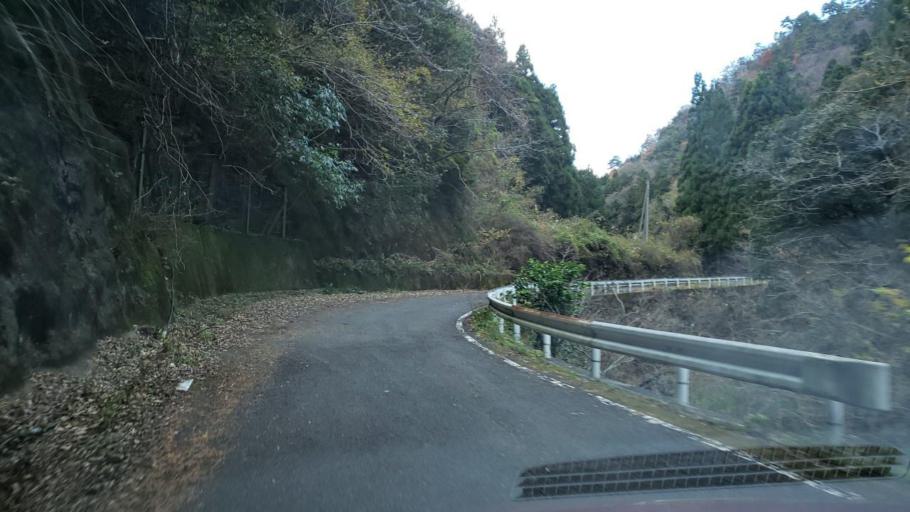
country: JP
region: Tokushima
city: Wakimachi
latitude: 34.1409
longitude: 134.2306
